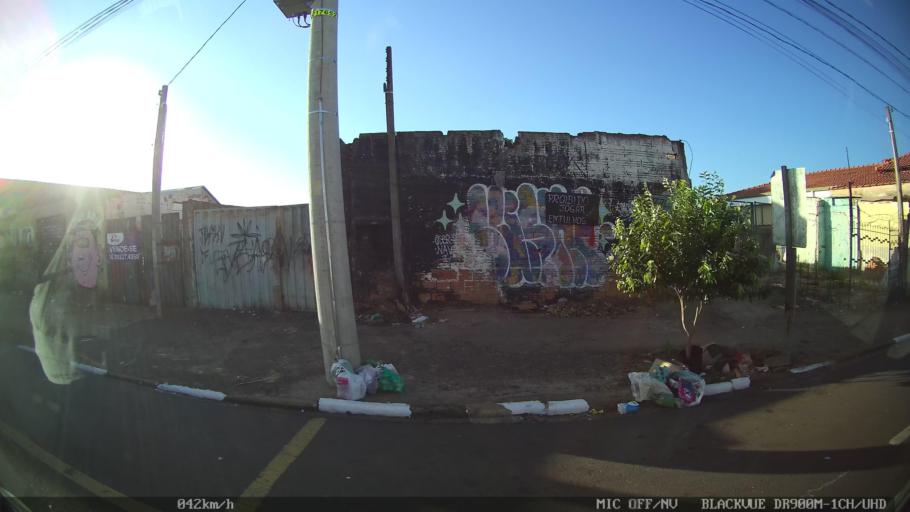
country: BR
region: Sao Paulo
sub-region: Franca
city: Franca
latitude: -20.5253
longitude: -47.3786
